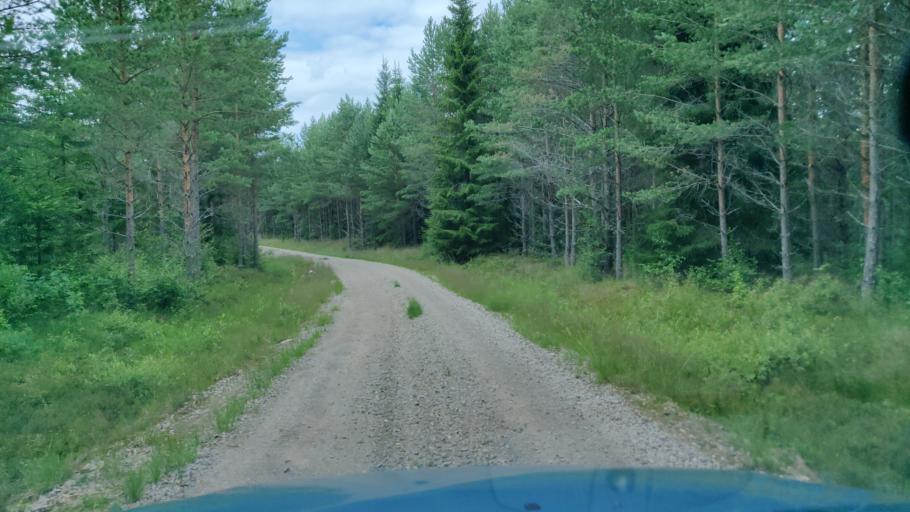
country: SE
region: Vaermland
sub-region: Hagfors Kommun
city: Hagfors
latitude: 59.9531
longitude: 13.5911
